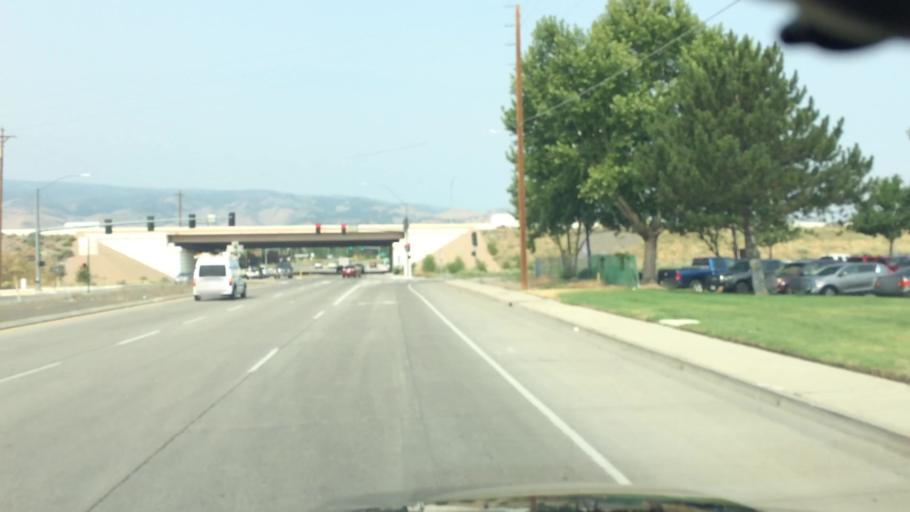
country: US
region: Nevada
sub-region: Washoe County
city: Reno
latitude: 39.4679
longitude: -119.7863
